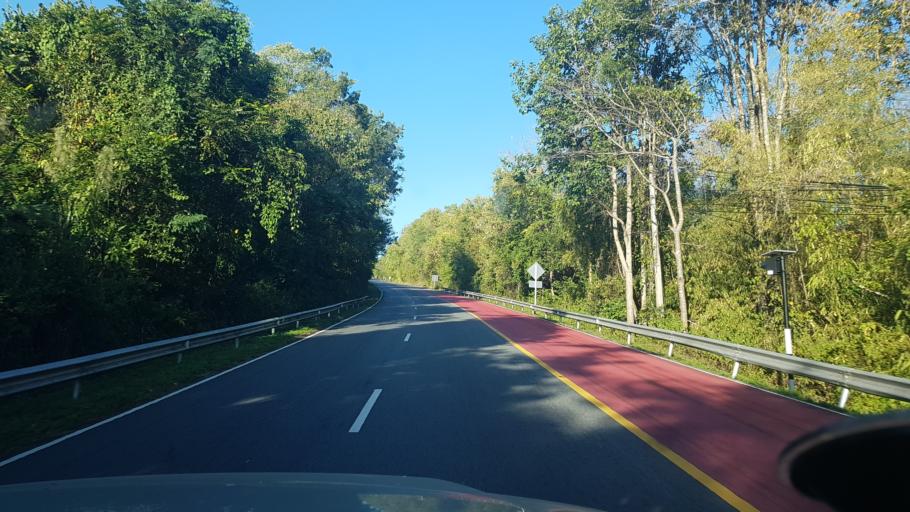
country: TH
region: Phetchabun
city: Nam Nao
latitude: 16.7030
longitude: 101.6581
